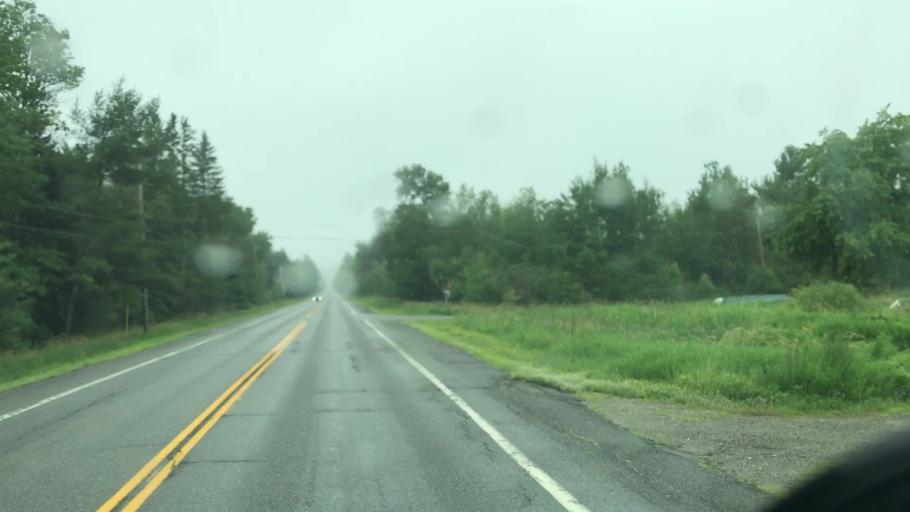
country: US
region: Maine
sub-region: Penobscot County
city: Howland
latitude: 45.2493
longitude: -68.6386
